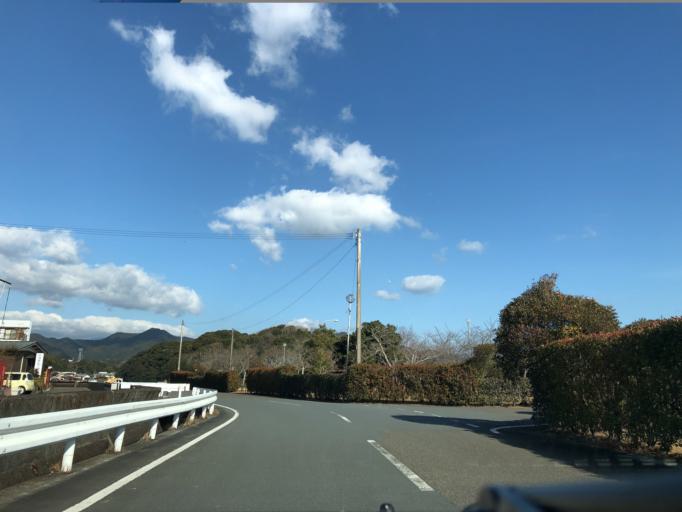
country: JP
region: Kochi
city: Sukumo
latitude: 32.9161
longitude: 132.7045
